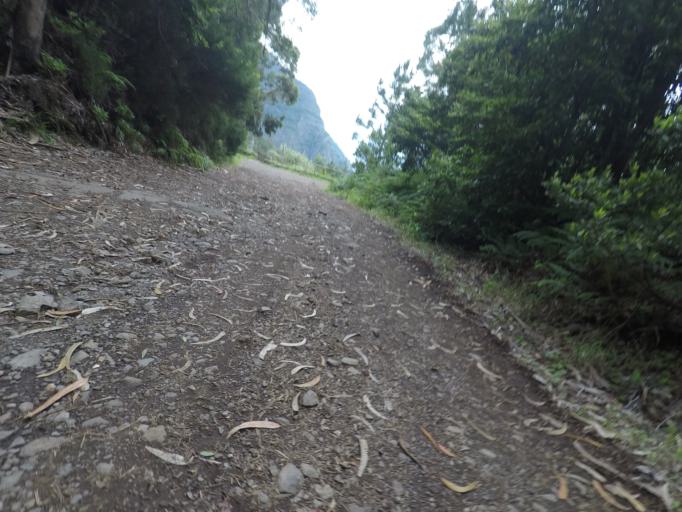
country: PT
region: Madeira
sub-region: Sao Vicente
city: Sao Vicente
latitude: 32.7779
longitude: -17.0481
